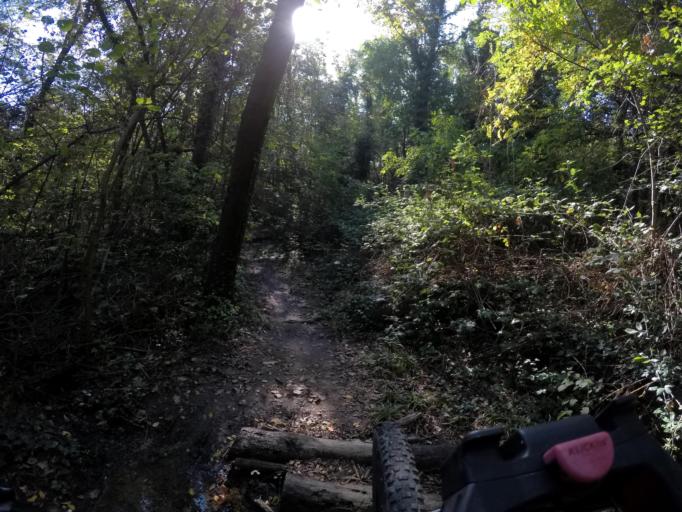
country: IT
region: Friuli Venezia Giulia
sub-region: Provincia di Udine
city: Manzano
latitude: 46.0063
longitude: 13.3812
